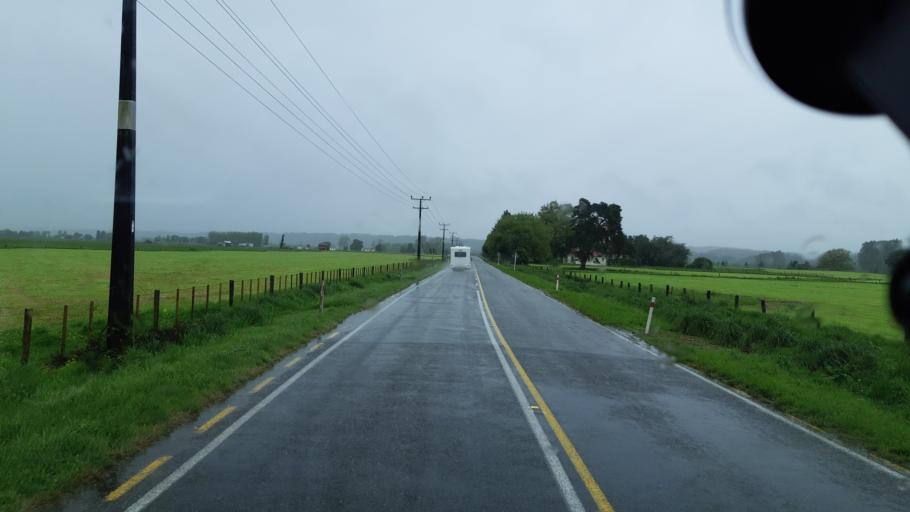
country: NZ
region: West Coast
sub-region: Grey District
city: Greymouth
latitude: -42.2950
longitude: 171.6354
